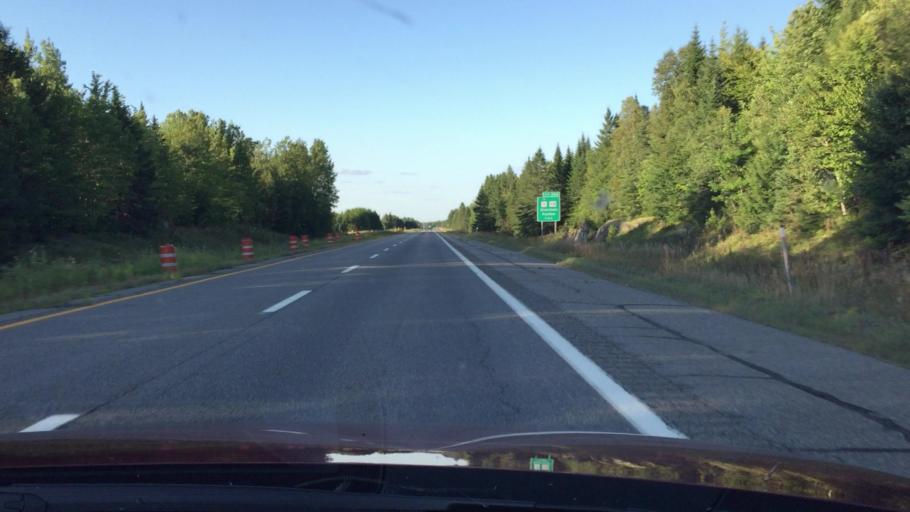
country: US
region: Maine
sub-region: Penobscot County
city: Patten
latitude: 45.8542
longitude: -68.4247
